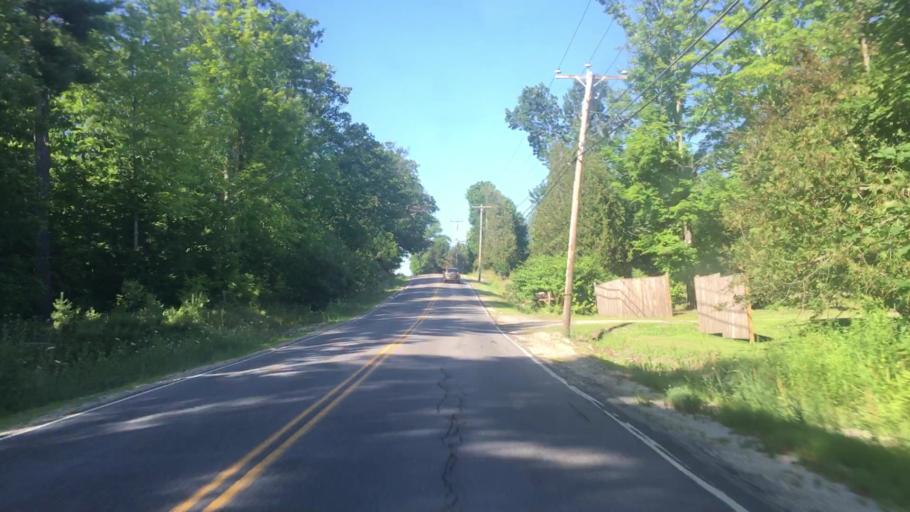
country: US
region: Maine
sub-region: York County
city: Buxton
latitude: 43.7084
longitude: -70.5743
